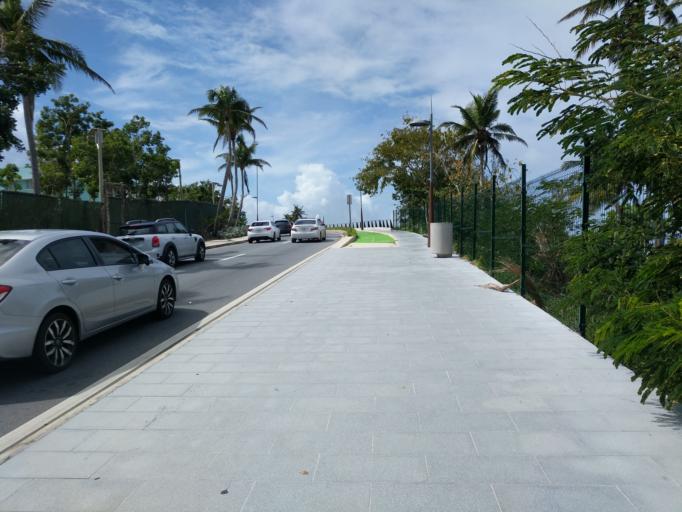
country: PR
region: San Juan
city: San Juan
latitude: 18.4660
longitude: -66.0940
